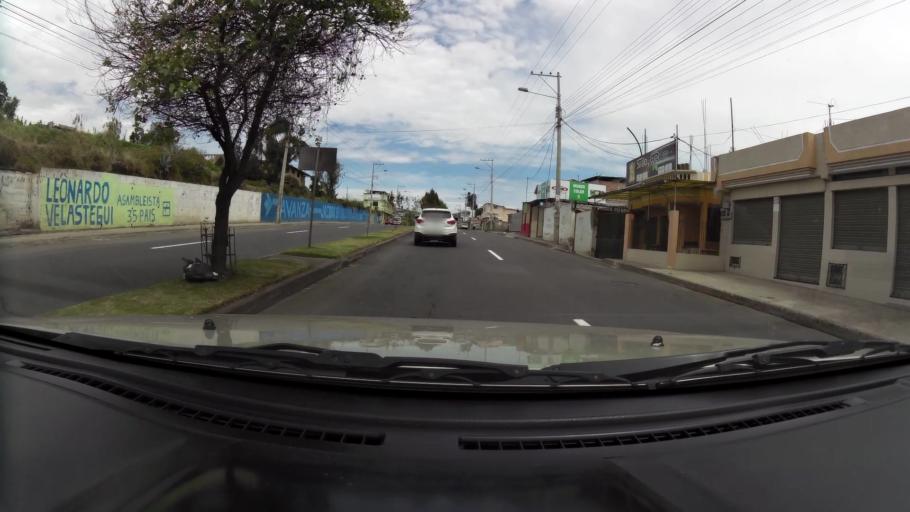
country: EC
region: Cotopaxi
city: San Miguel de Salcedo
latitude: -1.0813
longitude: -78.5949
